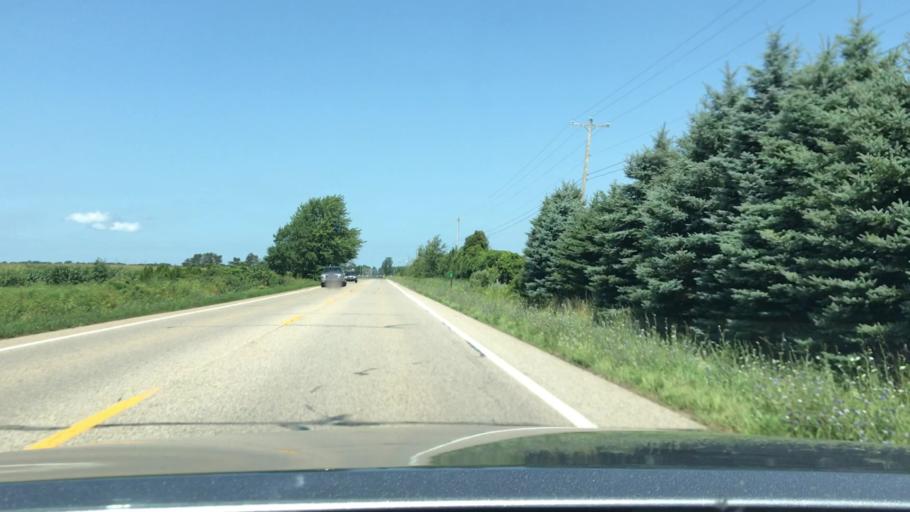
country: US
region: Michigan
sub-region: Ottawa County
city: Allendale
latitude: 42.9607
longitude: -86.0825
